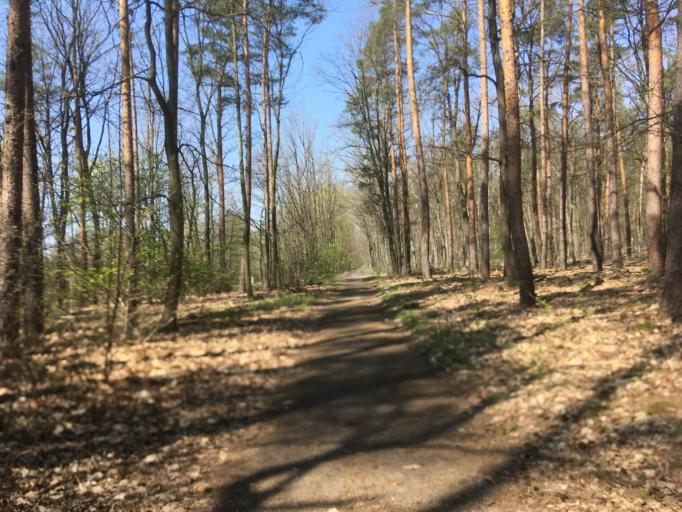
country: DE
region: Berlin
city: Grunewald
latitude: 52.4767
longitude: 13.2321
